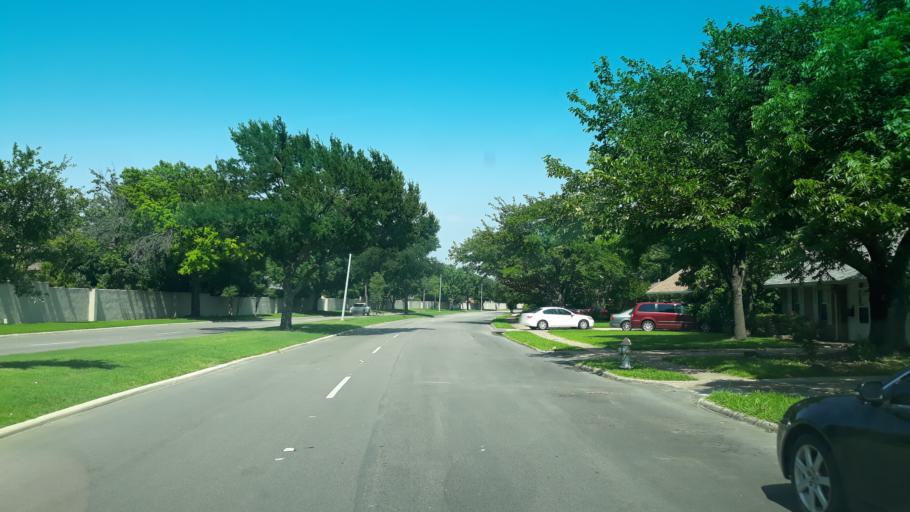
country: US
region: Texas
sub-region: Dallas County
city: Irving
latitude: 32.8563
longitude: -96.9717
